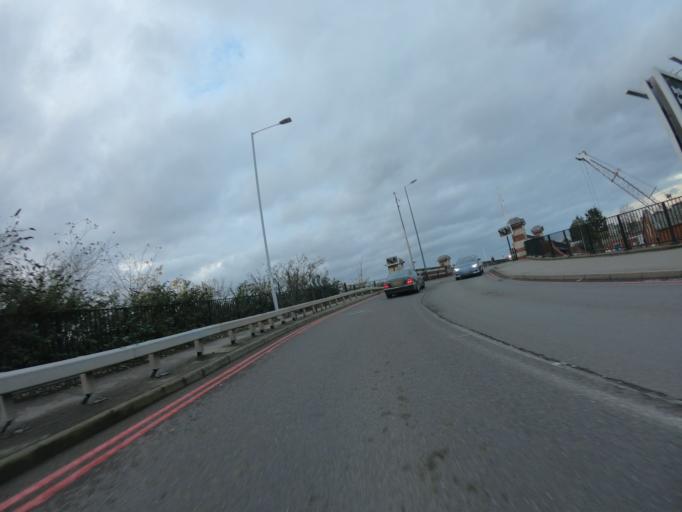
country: GB
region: England
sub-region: Greater London
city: Woolwich
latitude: 51.5023
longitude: 0.0702
